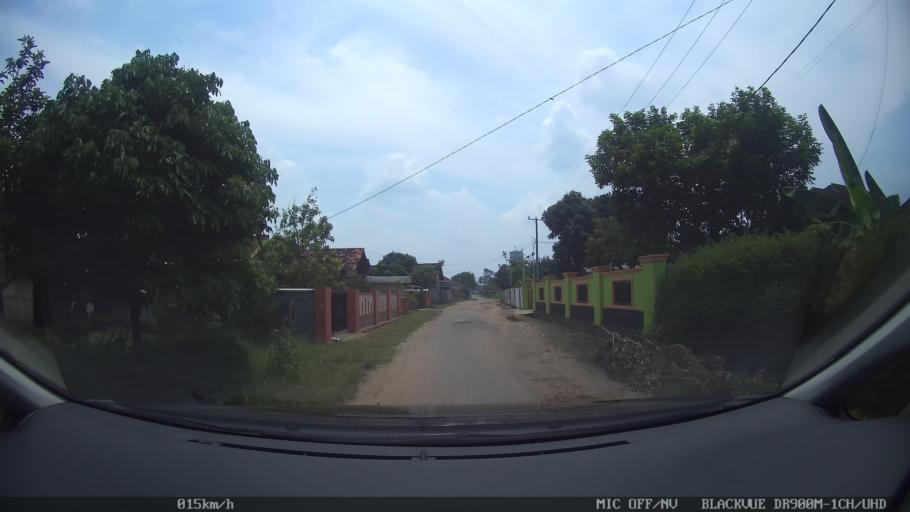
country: ID
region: Lampung
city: Natar
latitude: -5.3129
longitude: 105.2215
